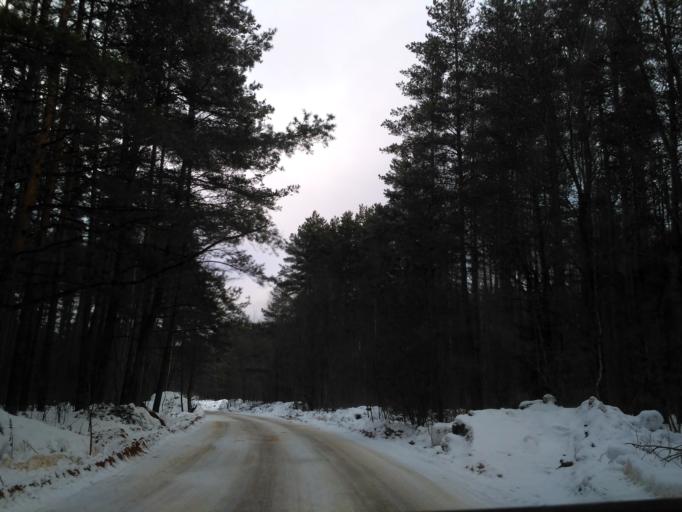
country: BY
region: Minsk
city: Vyaliki Trastsyanets
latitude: 53.9223
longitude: 27.7046
